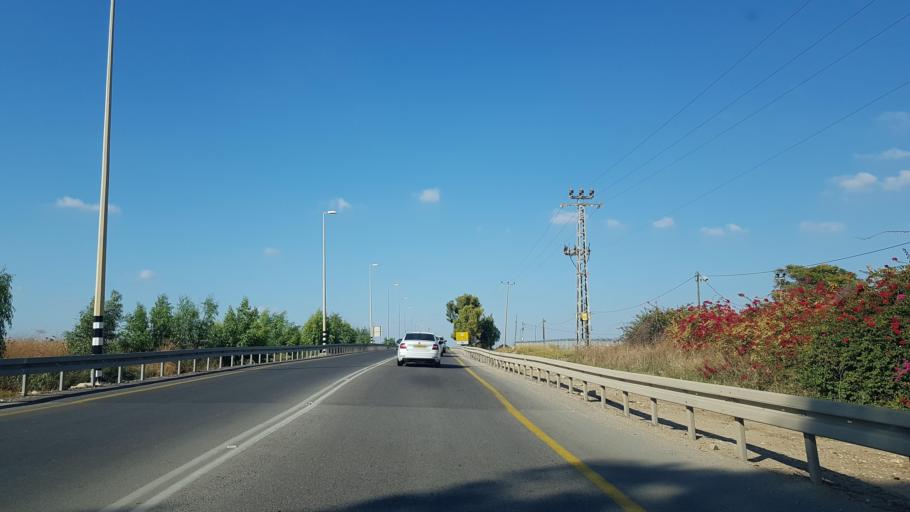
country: PS
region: West Bank
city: Tulkarm
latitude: 32.3395
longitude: 35.0099
